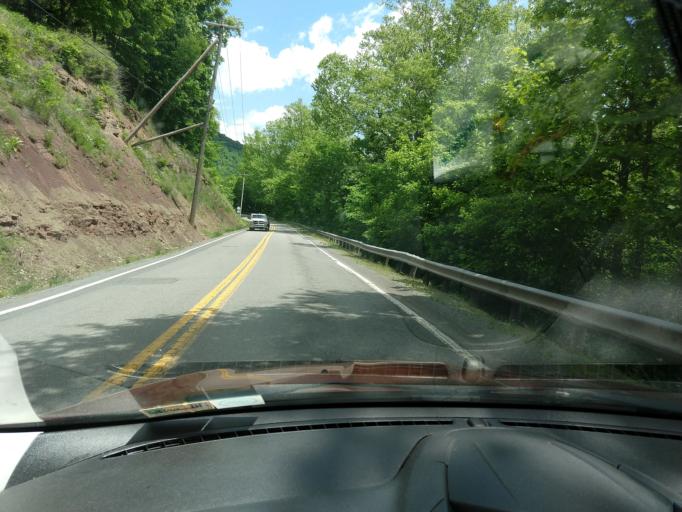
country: US
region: West Virginia
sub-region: Gilmer County
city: Glenville
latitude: 38.8668
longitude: -80.6885
